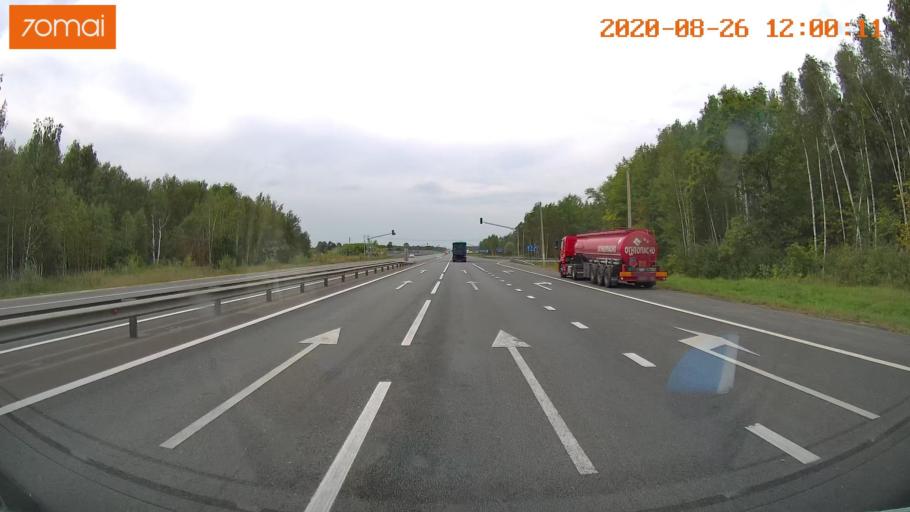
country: RU
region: Rjazan
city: Kiritsy
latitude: 54.2867
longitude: 40.2798
